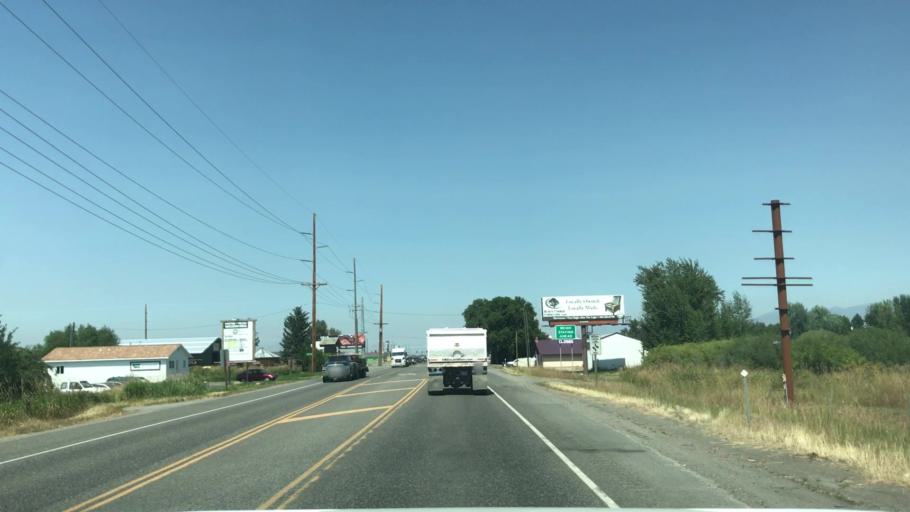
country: US
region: Montana
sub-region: Gallatin County
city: Four Corners
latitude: 45.6653
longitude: -111.1857
